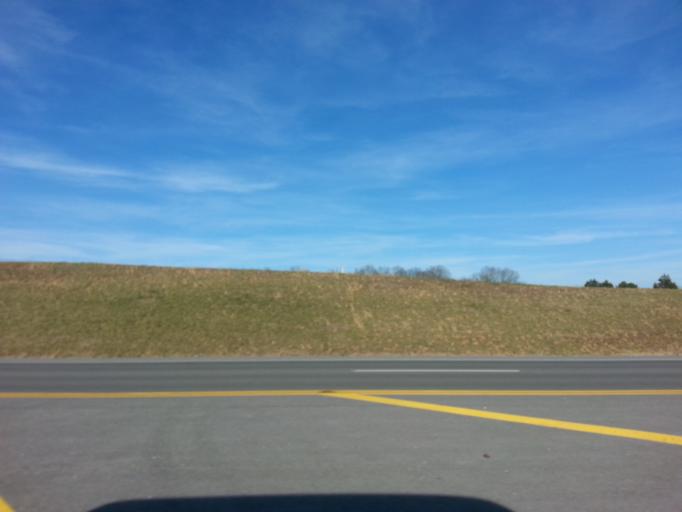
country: US
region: Tennessee
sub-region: Warren County
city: McMinnville
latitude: 35.7032
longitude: -85.8297
